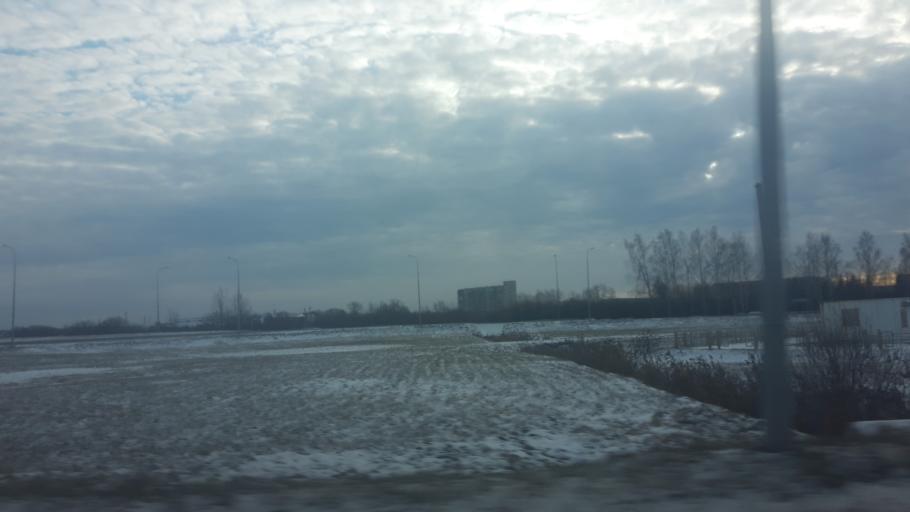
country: RU
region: Tjumen
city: Moskovskiy
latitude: 57.1869
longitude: 65.3583
